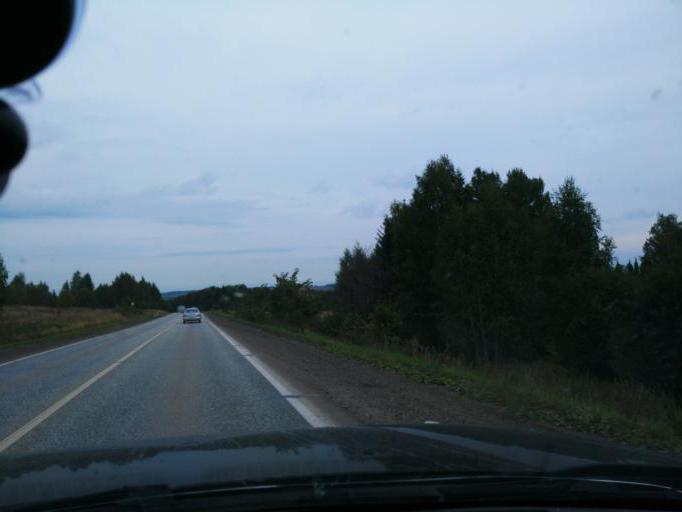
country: RU
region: Perm
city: Chernushka
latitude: 56.5890
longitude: 56.1515
